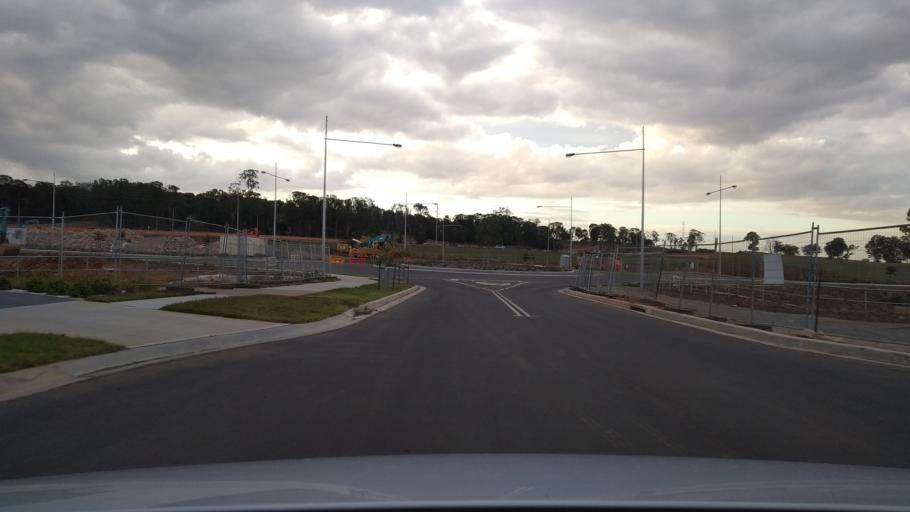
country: AU
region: New South Wales
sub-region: Camden
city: Narellan
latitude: -33.9967
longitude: 150.7287
